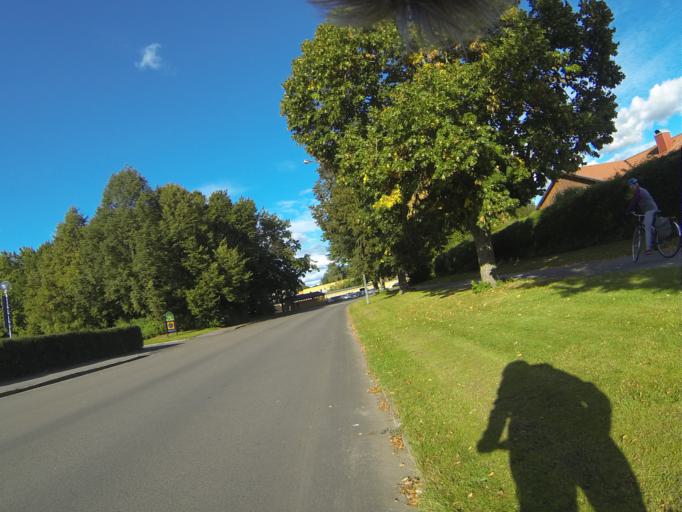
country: SE
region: Skane
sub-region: Lunds Kommun
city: Genarp
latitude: 55.7201
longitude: 13.3460
